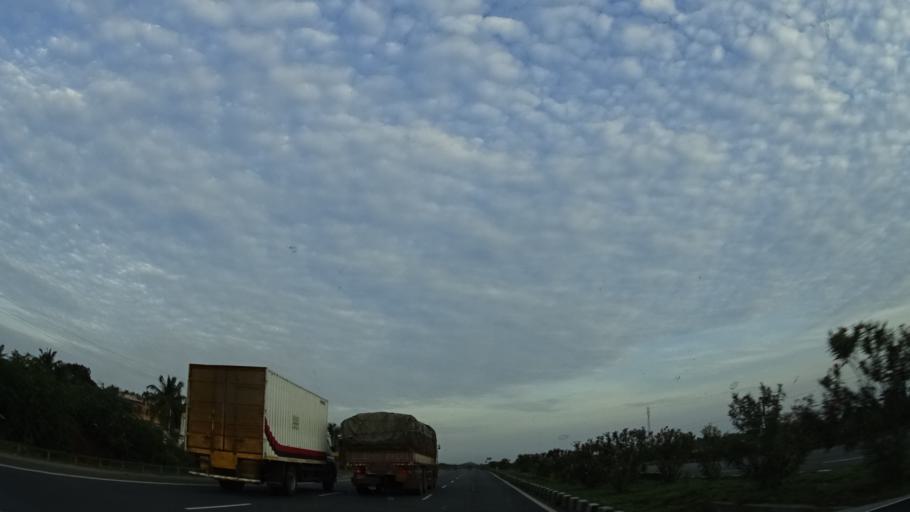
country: IN
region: Karnataka
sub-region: Tumkur
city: Sira
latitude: 13.8158
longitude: 76.7833
